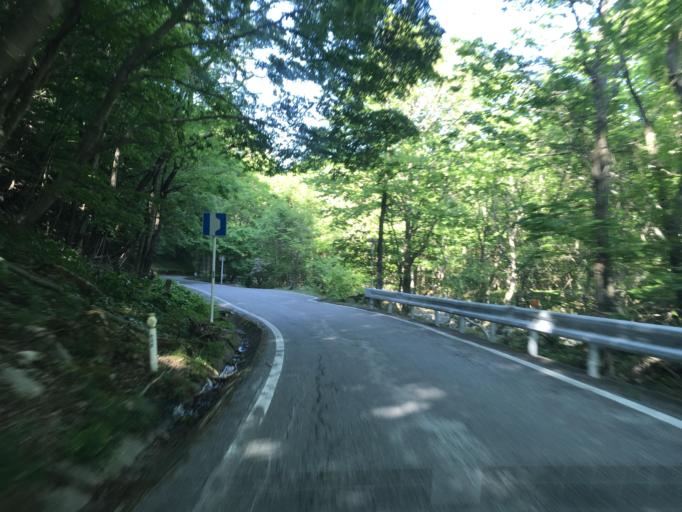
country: JP
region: Iwate
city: Ofunato
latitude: 39.1820
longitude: 141.7578
